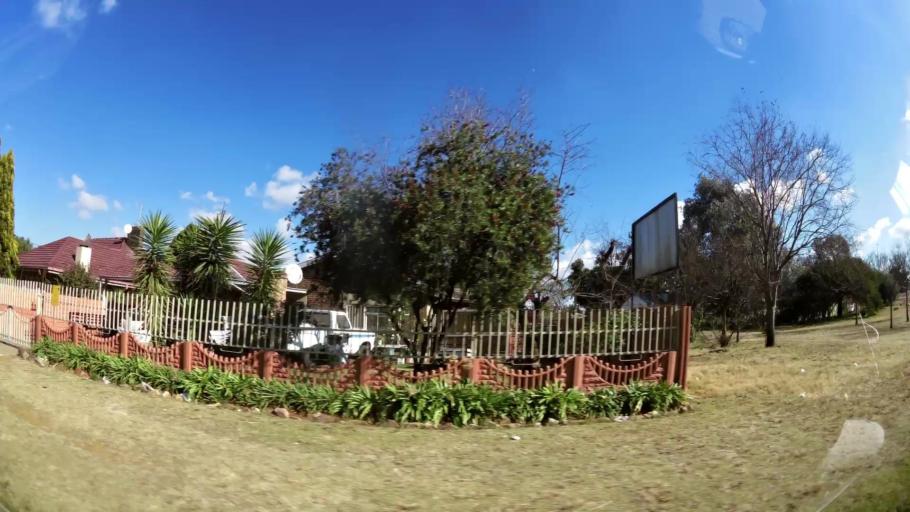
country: ZA
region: Gauteng
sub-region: City of Johannesburg Metropolitan Municipality
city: Roodepoort
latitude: -26.1334
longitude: 27.8378
